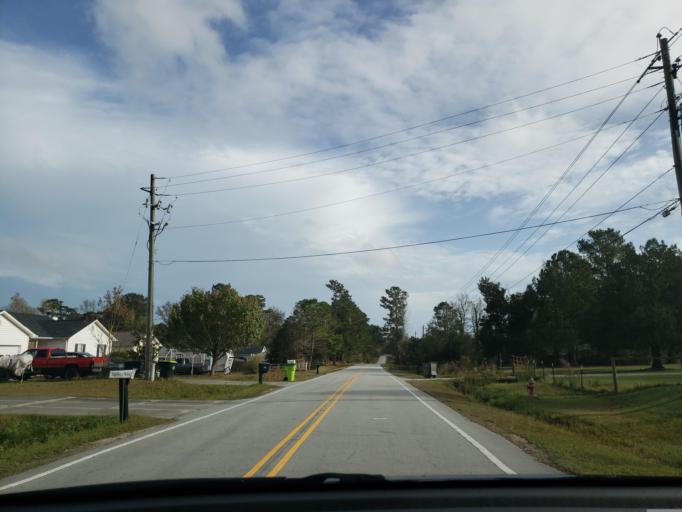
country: US
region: North Carolina
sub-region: Onslow County
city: Jacksonville
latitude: 34.6706
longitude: -77.4978
